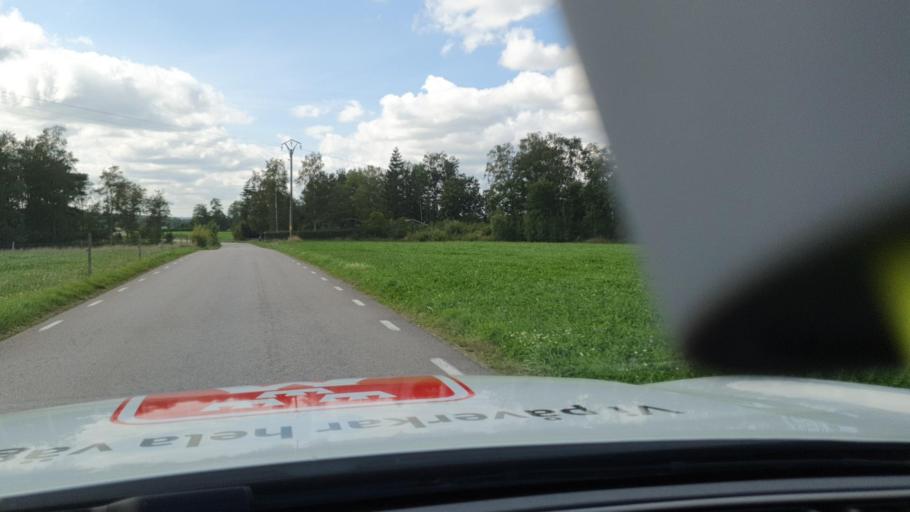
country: SE
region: Halland
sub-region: Laholms Kommun
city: Veinge
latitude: 56.4582
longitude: 13.1783
